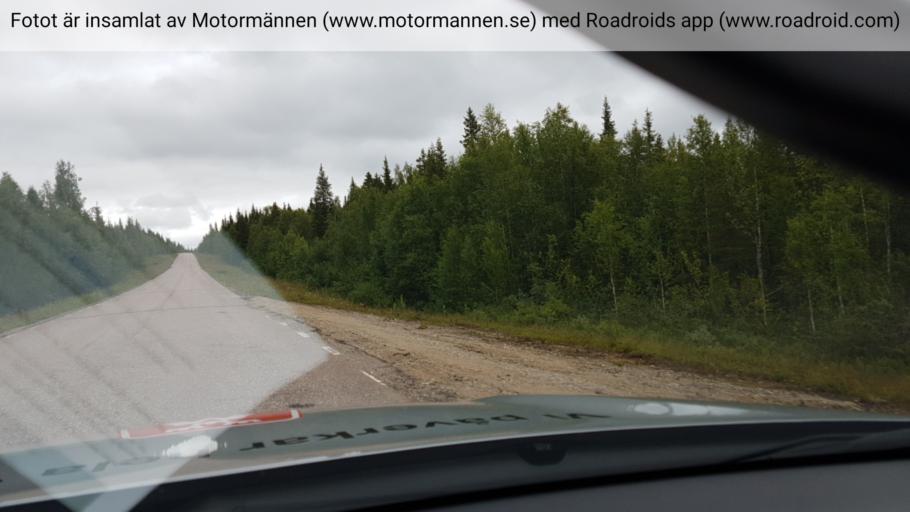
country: SE
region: Norrbotten
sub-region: Overkalix Kommun
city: OEverkalix
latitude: 67.0379
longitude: 22.0324
